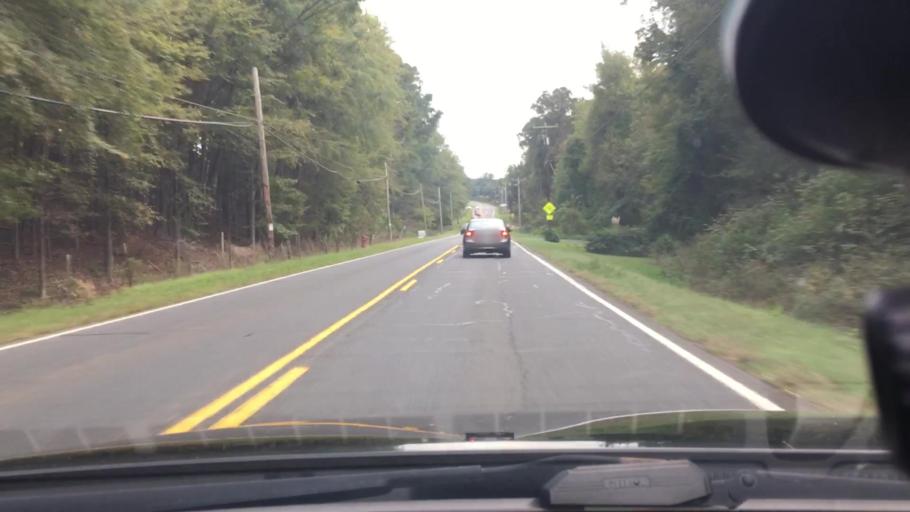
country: US
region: North Carolina
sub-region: Stanly County
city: Albemarle
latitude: 35.3346
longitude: -80.1351
